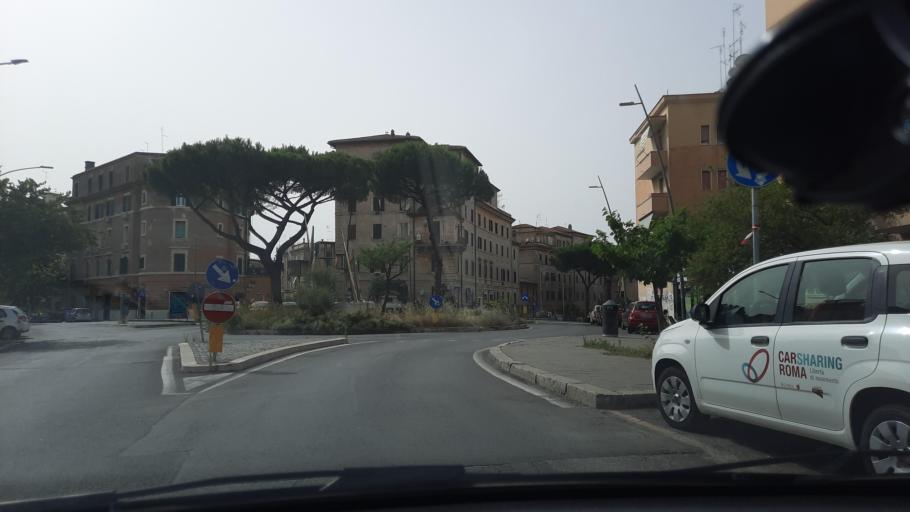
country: IT
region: Latium
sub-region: Citta metropolitana di Roma Capitale
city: Rome
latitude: 41.8609
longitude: 12.4864
